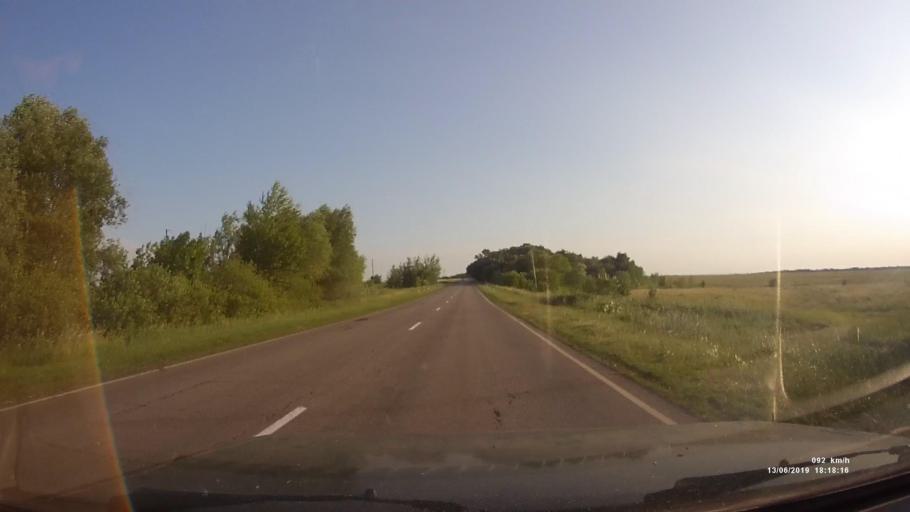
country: RU
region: Rostov
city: Kazanskaya
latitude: 49.9101
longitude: 41.3161
